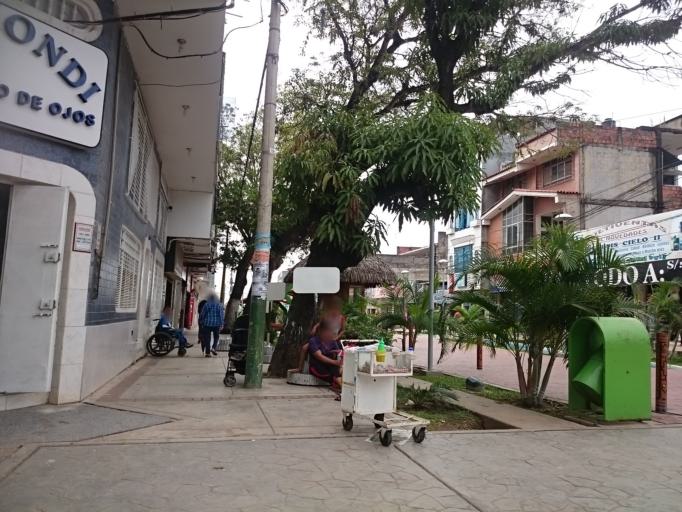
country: PE
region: Ucayali
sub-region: Provincia de Coronel Portillo
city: Pucallpa
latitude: -8.3852
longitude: -74.5303
